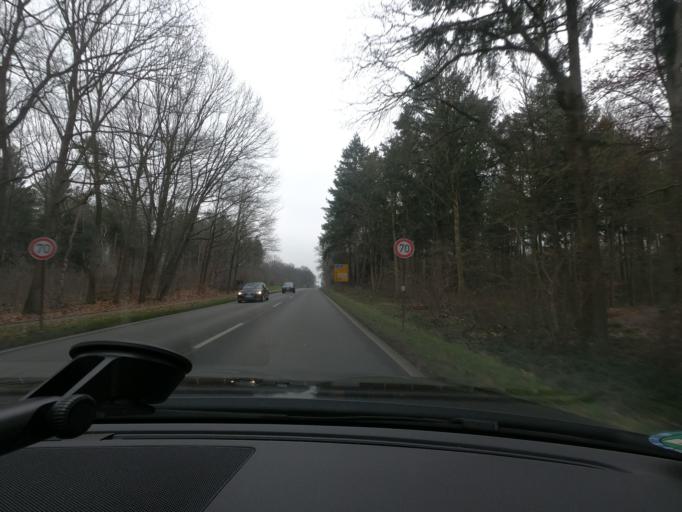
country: DE
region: North Rhine-Westphalia
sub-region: Regierungsbezirk Dusseldorf
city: Nettetal
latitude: 51.3530
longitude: 6.2365
